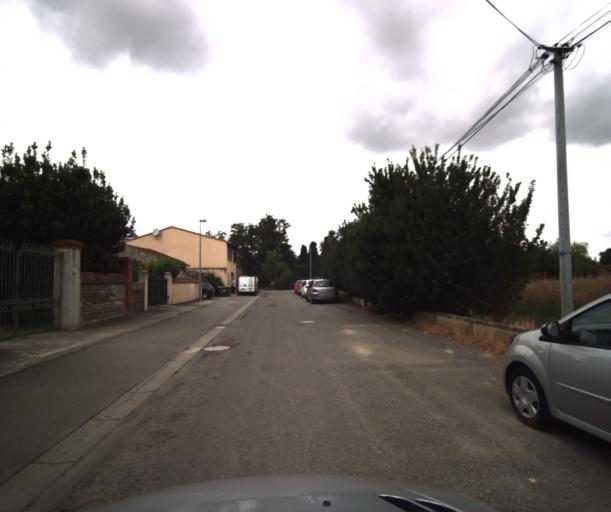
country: FR
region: Midi-Pyrenees
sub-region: Departement de la Haute-Garonne
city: Pinsaguel
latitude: 43.5093
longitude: 1.3907
